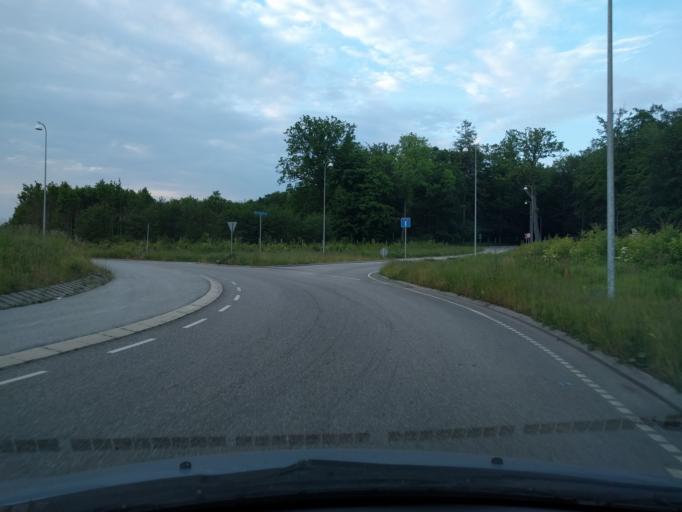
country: DK
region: Zealand
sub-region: Naestved Kommune
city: Naestved
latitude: 55.2316
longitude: 11.7985
